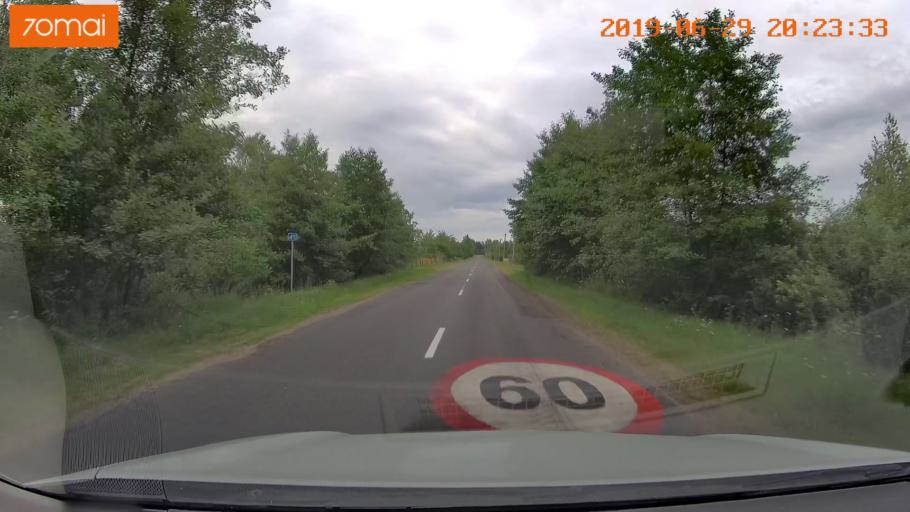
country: BY
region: Brest
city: Asnyezhytsy
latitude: 52.4459
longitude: 26.2613
